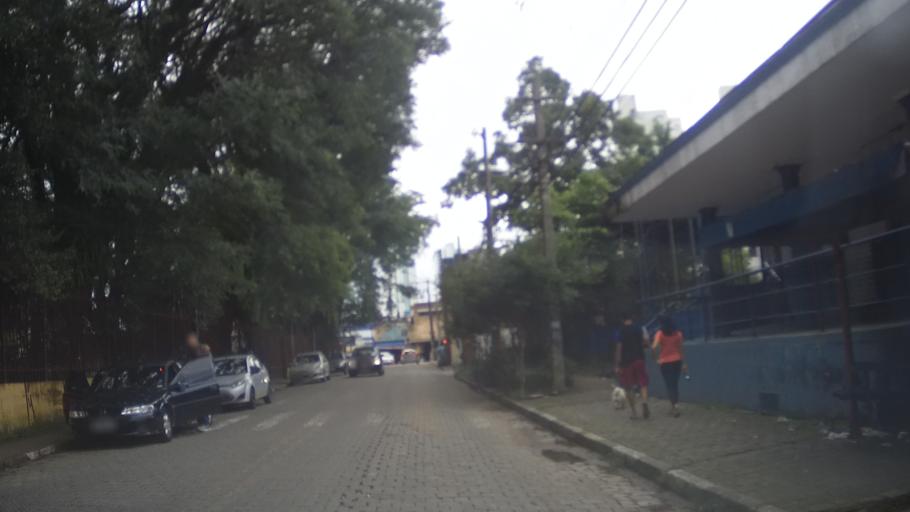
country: BR
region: Sao Paulo
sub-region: Guarulhos
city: Guarulhos
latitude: -23.4663
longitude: -46.5490
